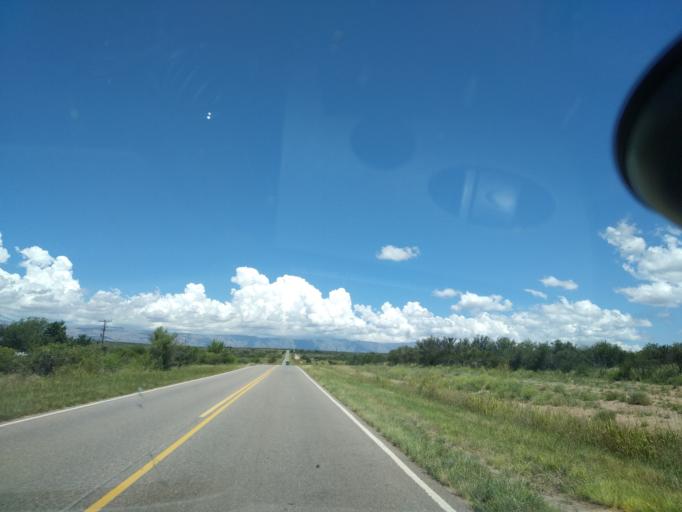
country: AR
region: Cordoba
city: Villa Cura Brochero
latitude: -31.6772
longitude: -65.0870
